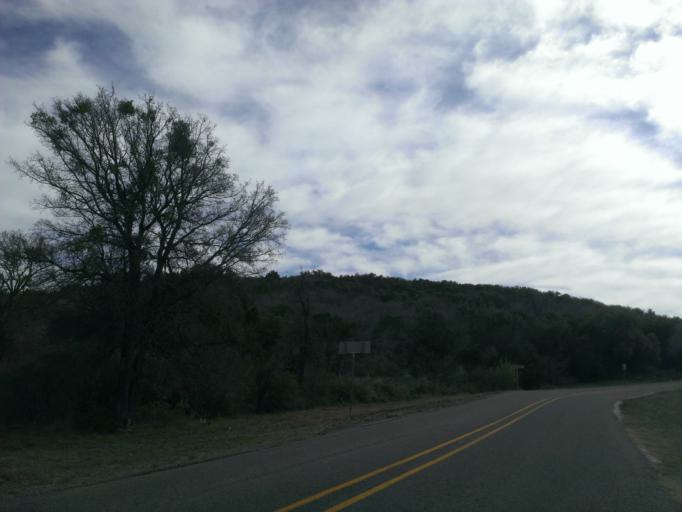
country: US
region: Texas
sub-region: Llano County
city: Buchanan Dam
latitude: 30.7003
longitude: -98.3807
